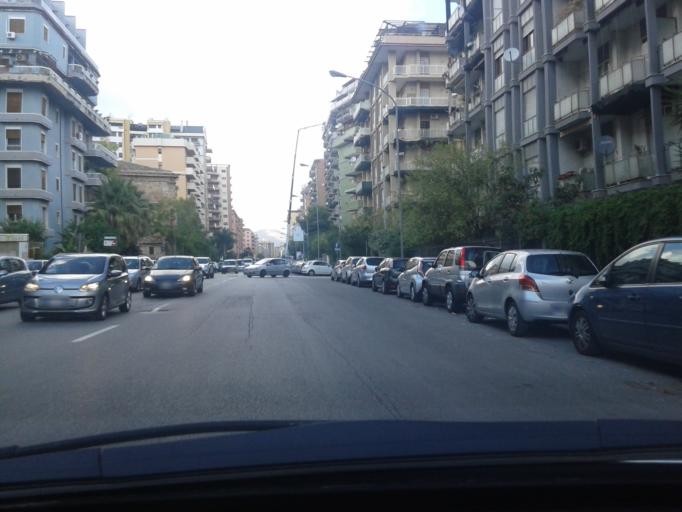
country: IT
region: Sicily
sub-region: Palermo
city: Palermo
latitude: 38.1483
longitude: 13.3303
